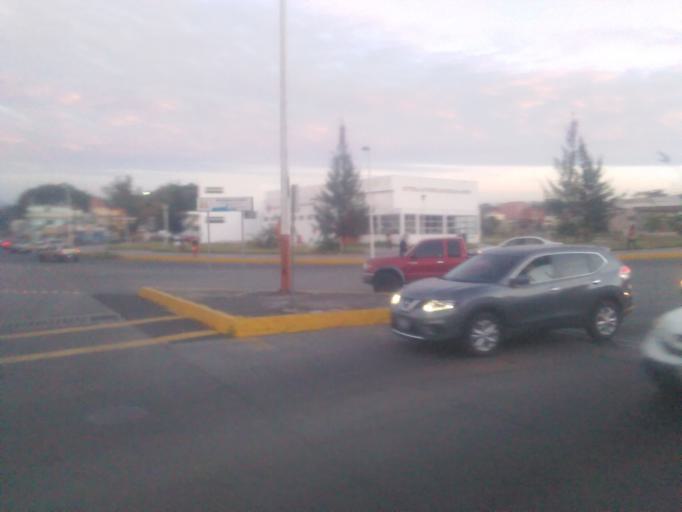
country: MX
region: Nayarit
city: Tepic
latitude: 21.5127
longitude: -104.9029
